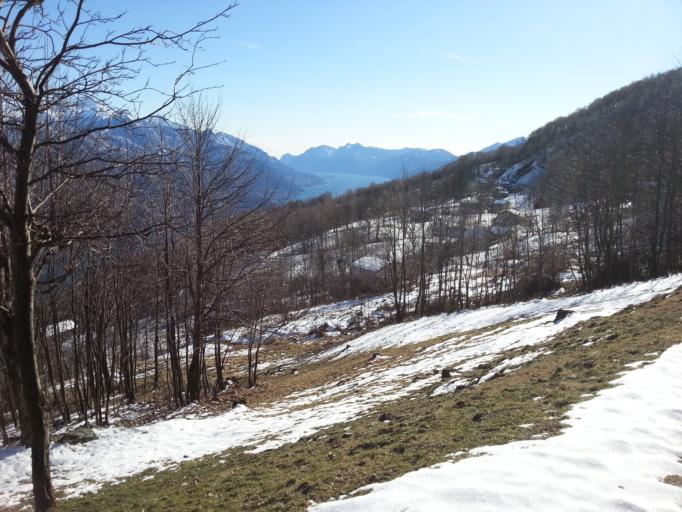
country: IT
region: Lombardy
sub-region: Provincia di Como
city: San Siro
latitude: 46.0744
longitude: 9.2475
